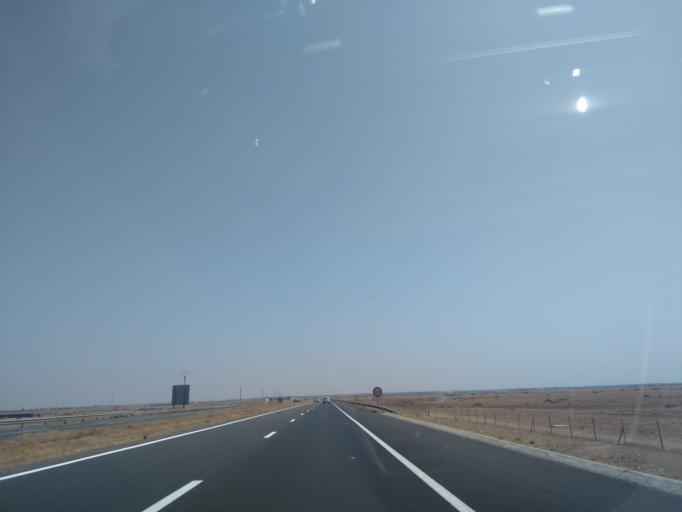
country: MA
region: Marrakech-Tensift-Al Haouz
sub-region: Kelaa-Des-Sraghna
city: Sidi Bou Othmane
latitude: 31.9250
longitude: -8.0216
